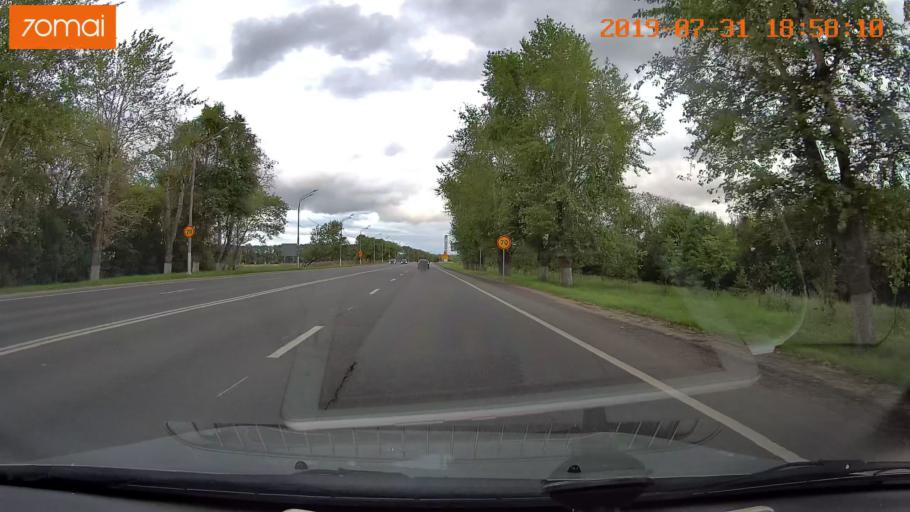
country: RU
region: Moskovskaya
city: Raduzhnyy
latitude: 55.1487
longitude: 38.7011
